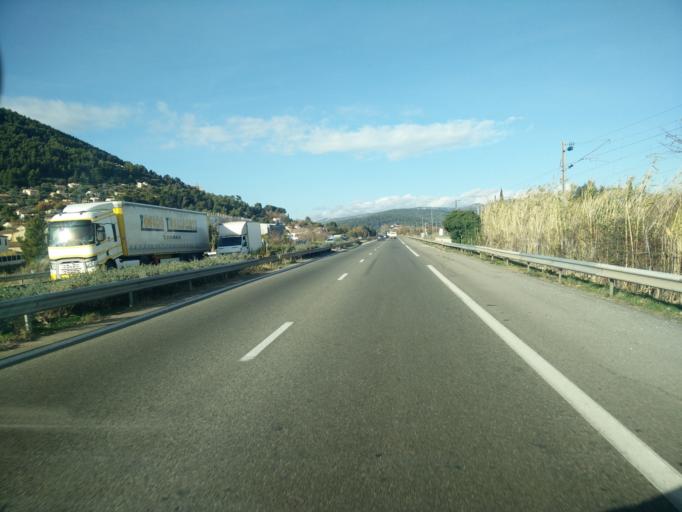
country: FR
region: Provence-Alpes-Cote d'Azur
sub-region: Departement du Var
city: La Farlede
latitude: 43.1715
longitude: 6.0501
